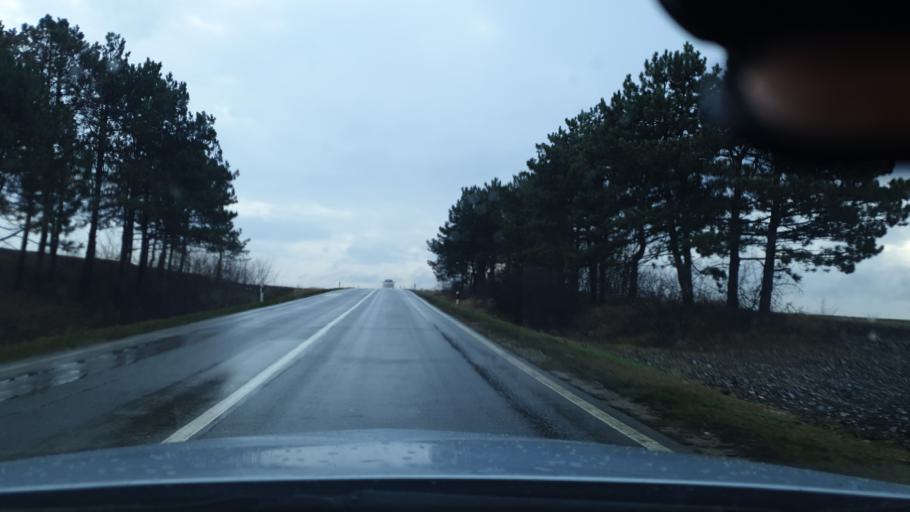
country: RS
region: Autonomna Pokrajina Vojvodina
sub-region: Juznobanatski Okrug
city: Kovin
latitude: 44.8311
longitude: 20.8309
